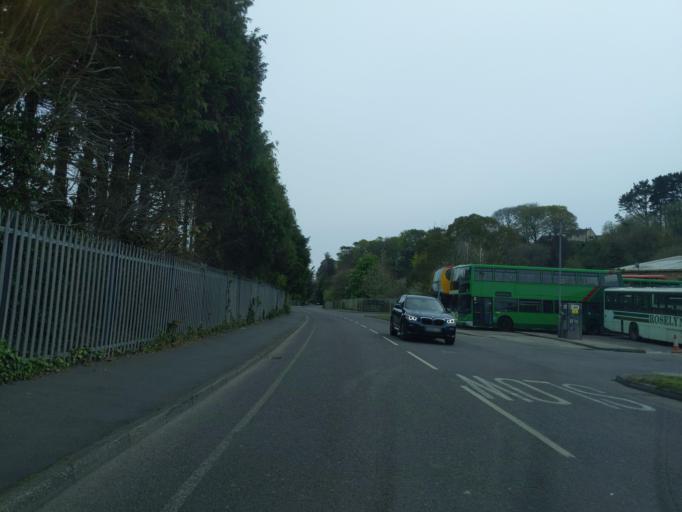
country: GB
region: England
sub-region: Cornwall
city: Par
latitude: 50.3565
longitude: -4.7122
